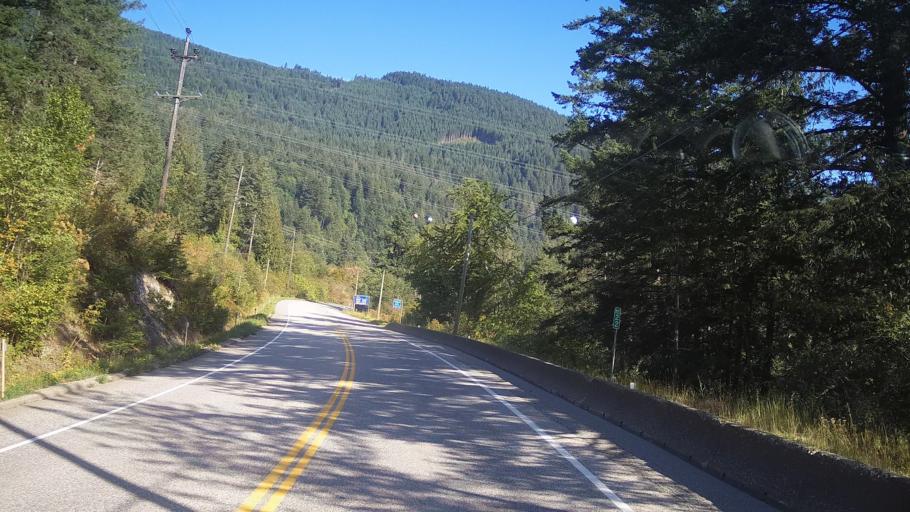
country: CA
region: British Columbia
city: Hope
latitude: 49.5494
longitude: -121.4419
